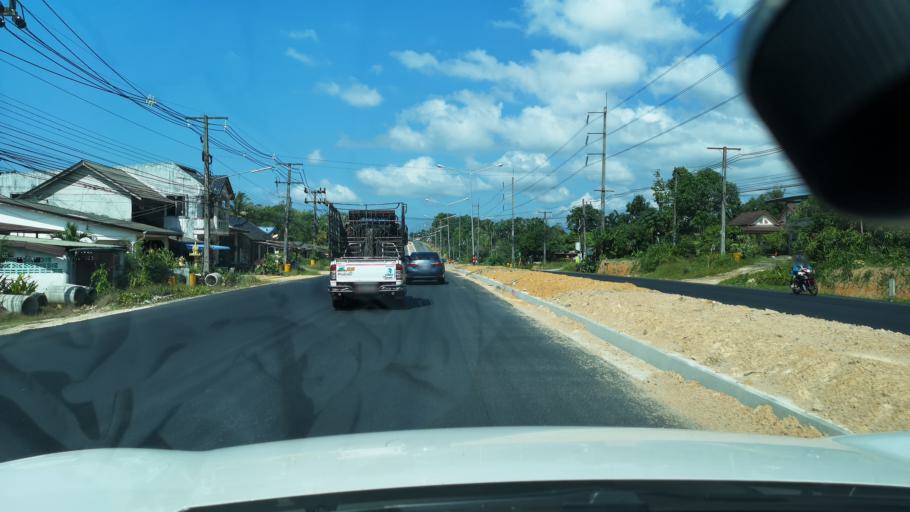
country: TH
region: Phangnga
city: Thai Mueang
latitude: 8.4239
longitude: 98.2587
